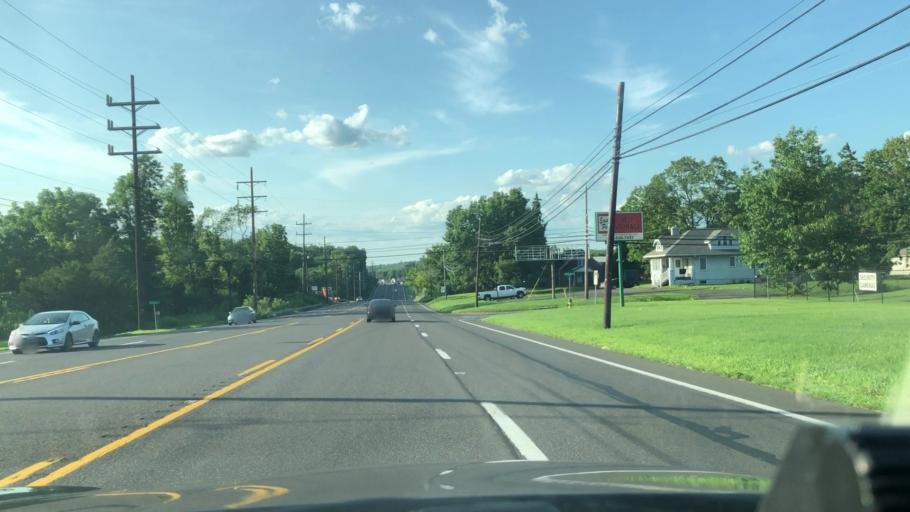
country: US
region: Pennsylvania
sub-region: Bucks County
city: Quakertown
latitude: 40.4642
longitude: -75.3695
